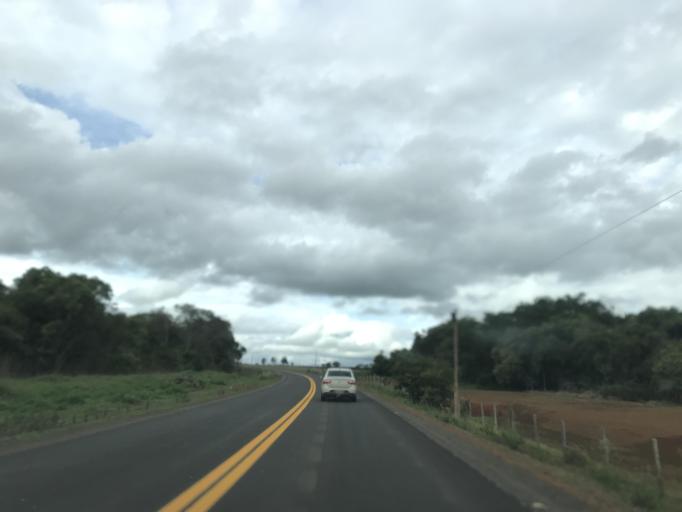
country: BR
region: Goias
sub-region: Bela Vista De Goias
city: Bela Vista de Goias
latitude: -17.0928
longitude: -48.6543
